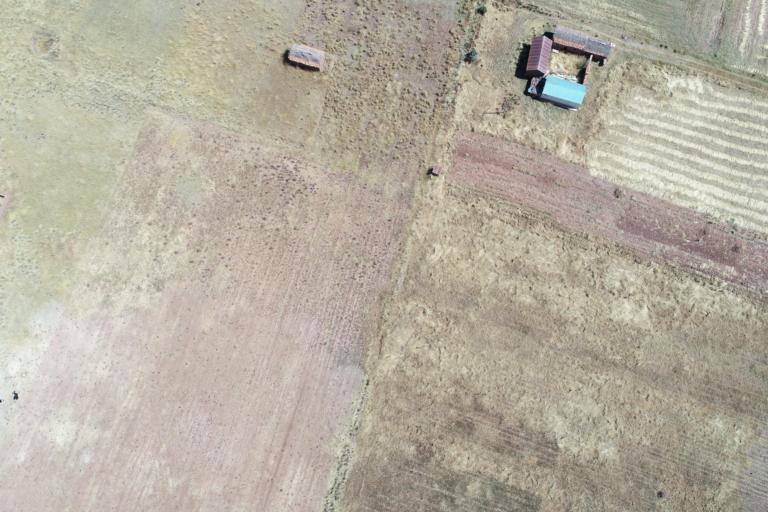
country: BO
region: La Paz
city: Tiahuanaco
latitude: -16.5949
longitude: -68.7730
